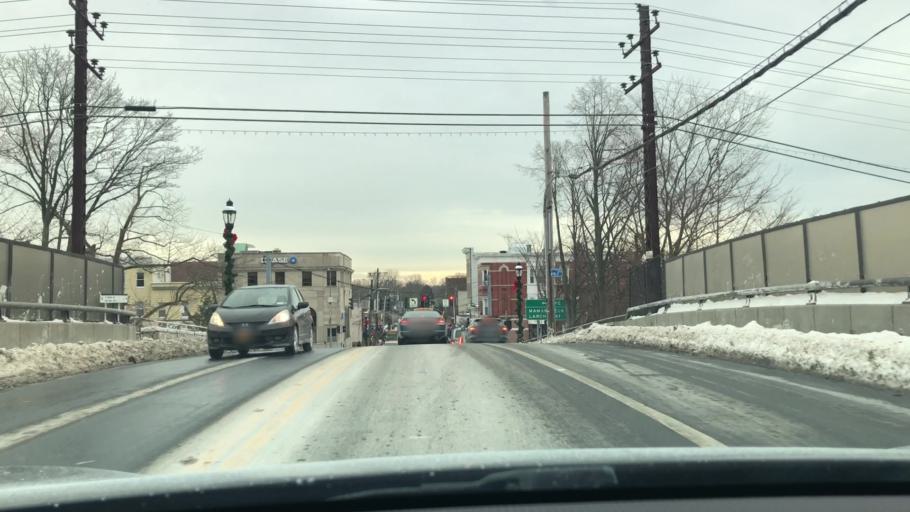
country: US
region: New York
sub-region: Westchester County
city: Harrison
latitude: 40.9696
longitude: -73.7130
